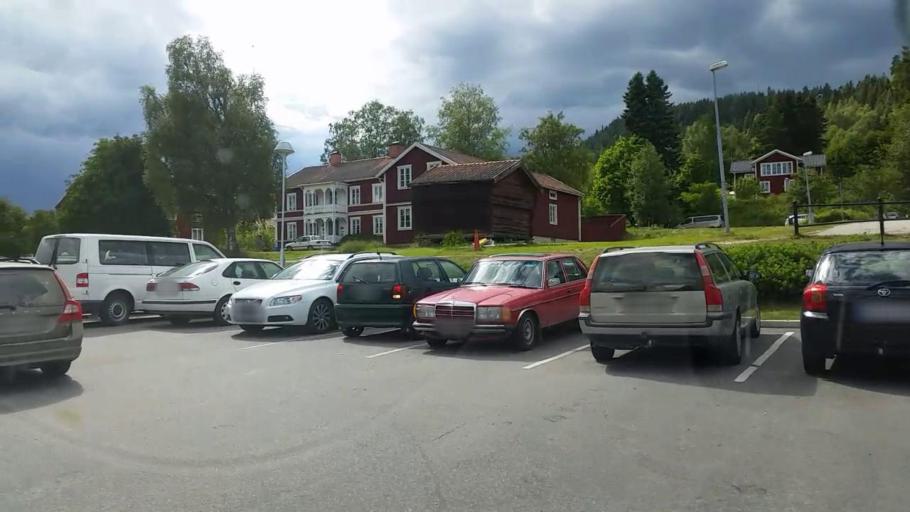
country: SE
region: Gaevleborg
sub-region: Ljusdals Kommun
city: Jaervsoe
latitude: 61.7175
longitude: 16.1694
